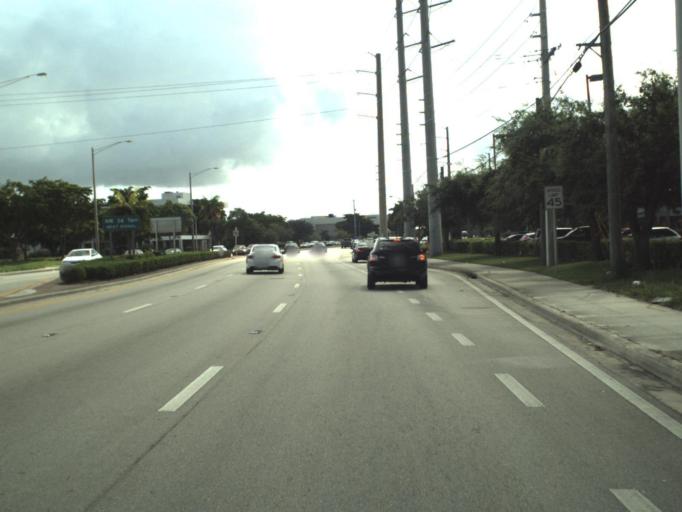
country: US
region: Florida
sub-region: Broward County
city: Lauderdale Lakes
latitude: 26.1648
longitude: -80.2015
